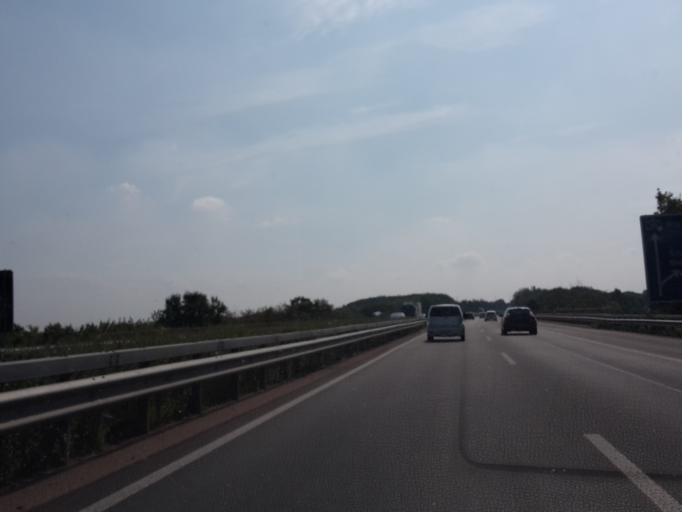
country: DE
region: Rheinland-Pfalz
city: Sorgenloch
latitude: 49.8977
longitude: 8.1885
